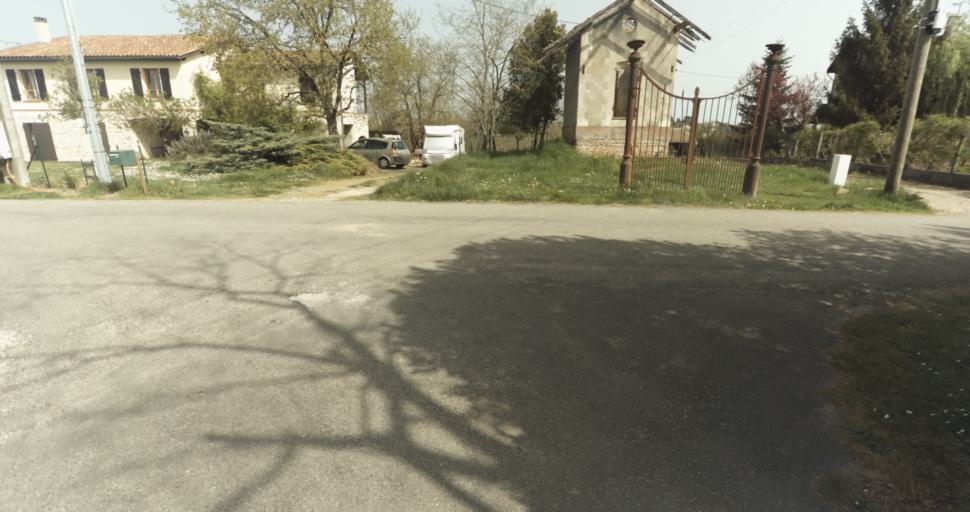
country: FR
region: Midi-Pyrenees
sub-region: Departement du Tarn-et-Garonne
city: Moissac
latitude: 44.1065
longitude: 1.0778
